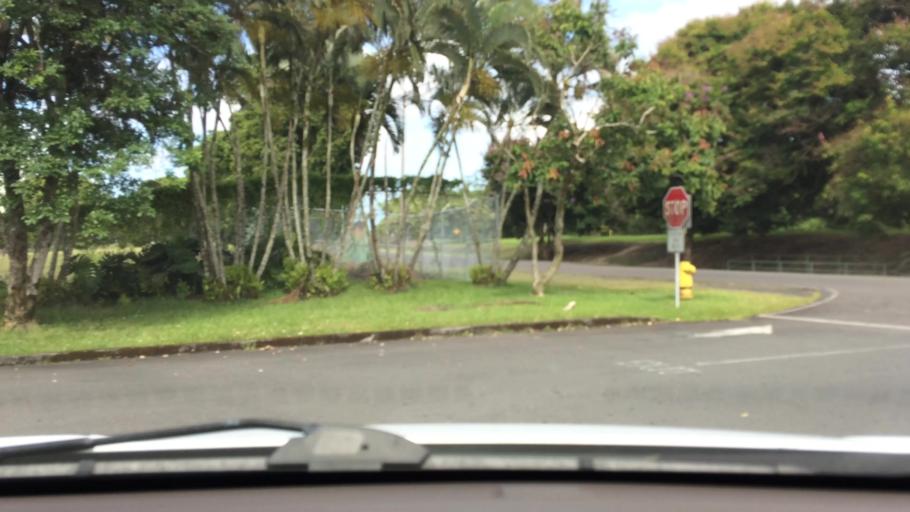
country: US
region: Hawaii
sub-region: Hawaii County
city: Hilo
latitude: 19.7158
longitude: -155.0500
